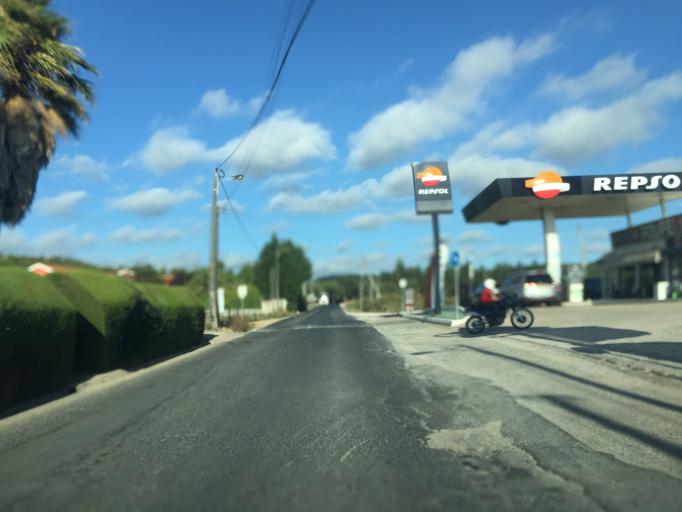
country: PT
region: Lisbon
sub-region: Torres Vedras
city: A dos Cunhados
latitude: 39.1458
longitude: -9.2824
